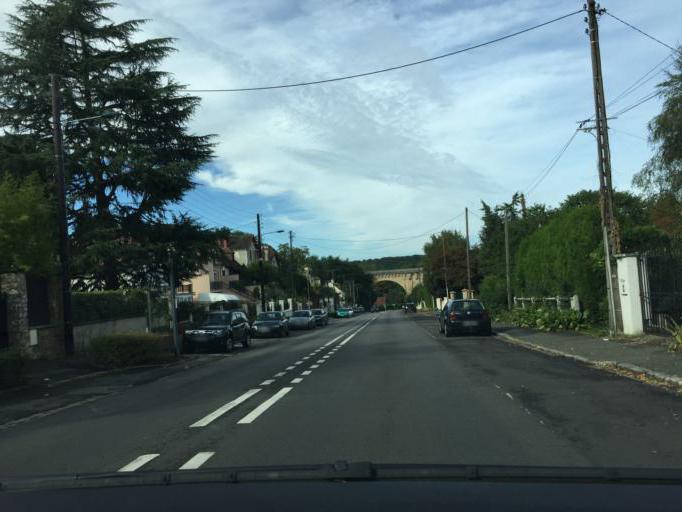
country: FR
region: Ile-de-France
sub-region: Departement de l'Essonne
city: Orsay
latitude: 48.6900
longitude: 2.1814
